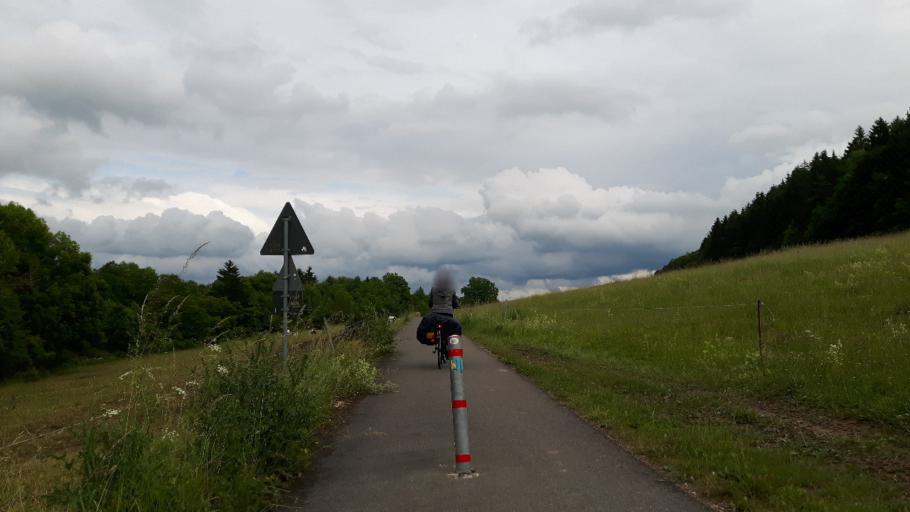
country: DE
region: Thuringia
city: Hildburghausen
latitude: 50.4154
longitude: 10.7526
